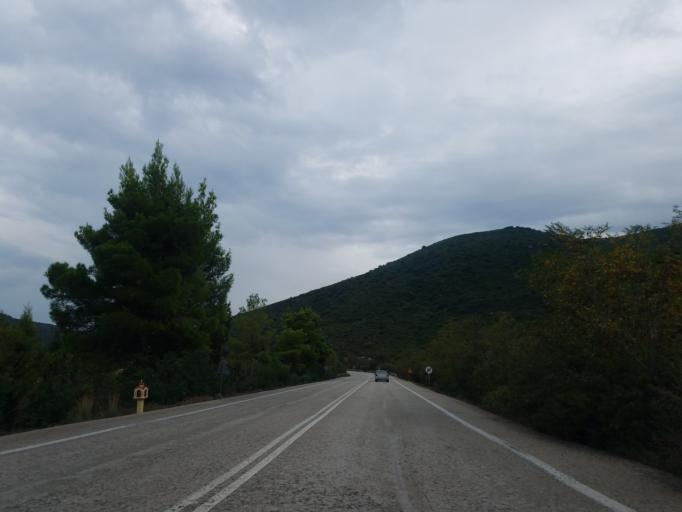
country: GR
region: Central Greece
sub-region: Nomos Voiotias
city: Livadeia
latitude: 38.4489
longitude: 22.7897
